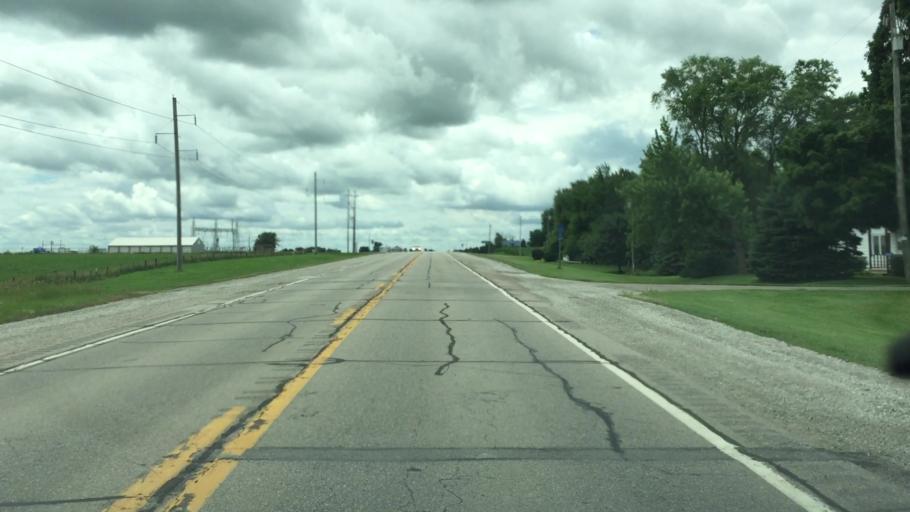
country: US
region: Iowa
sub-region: Jasper County
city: Monroe
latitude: 41.5757
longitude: -93.0971
